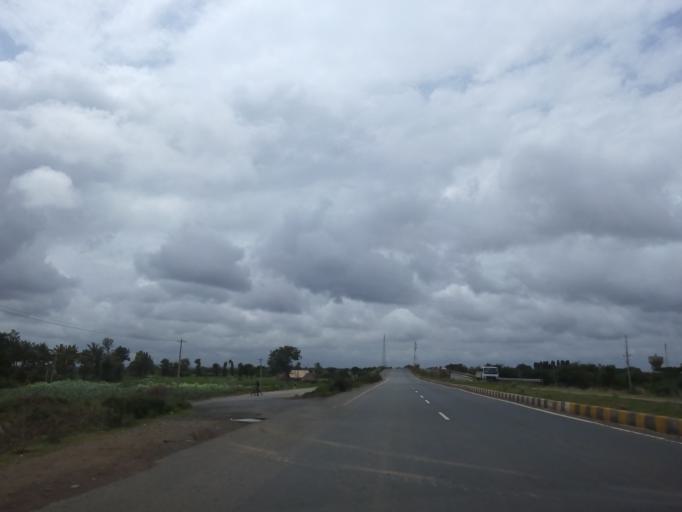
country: IN
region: Karnataka
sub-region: Haveri
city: Byadgi
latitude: 14.6835
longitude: 75.5419
